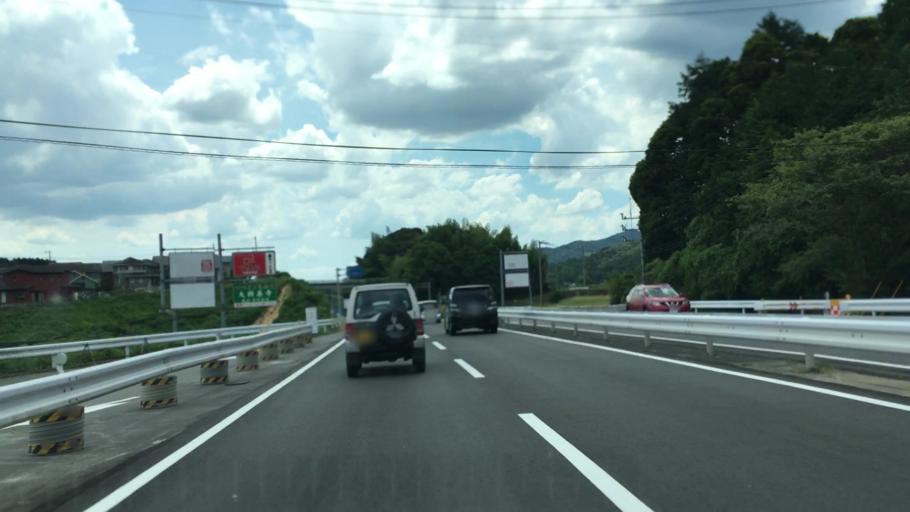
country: JP
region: Fukuoka
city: Chikushino-shi
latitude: 33.4400
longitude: 130.5265
